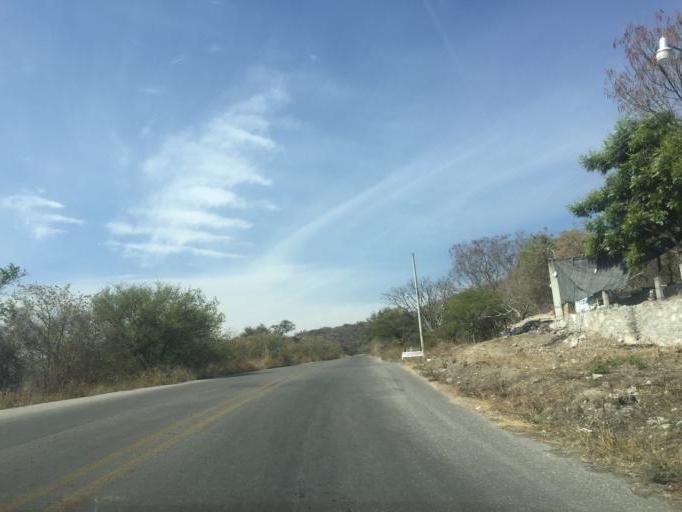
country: MX
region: Morelos
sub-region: Miacatlan
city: Xochicalco (Cirenio Longares)
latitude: 18.7950
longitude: -99.2982
